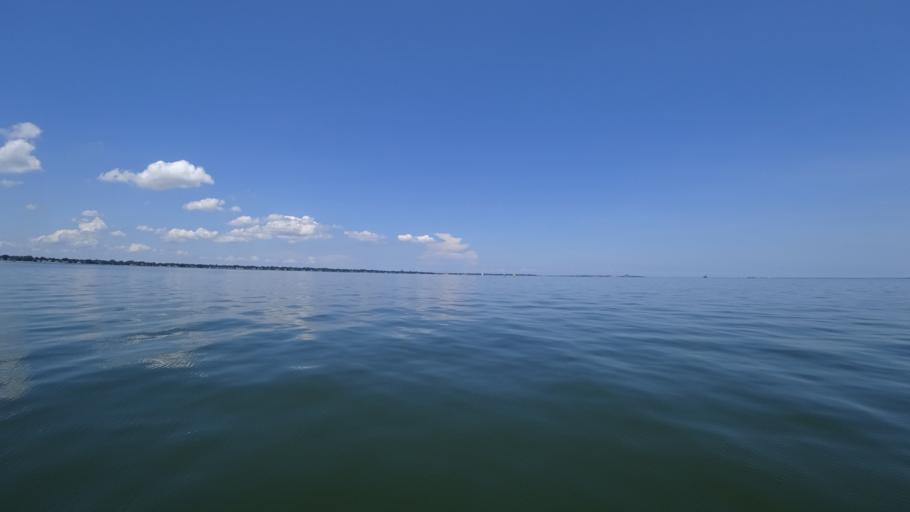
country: US
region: Virginia
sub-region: City of Newport News
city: Newport News
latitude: 36.9729
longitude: -76.3718
